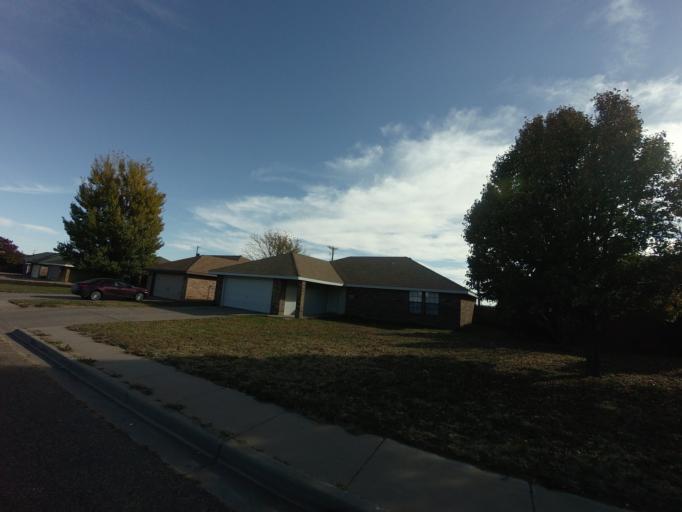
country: US
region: New Mexico
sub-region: Curry County
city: Clovis
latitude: 34.4129
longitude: -103.1686
